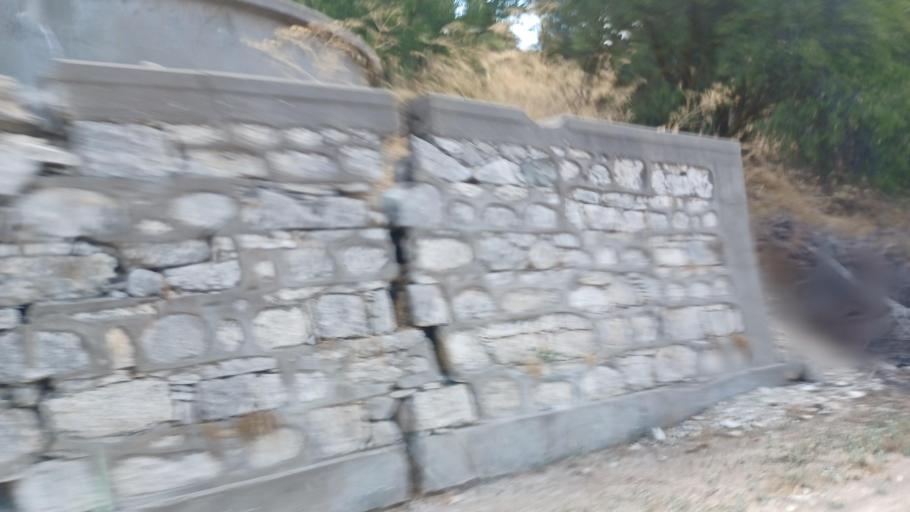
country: CY
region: Pafos
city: Mesogi
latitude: 34.8832
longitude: 32.6101
